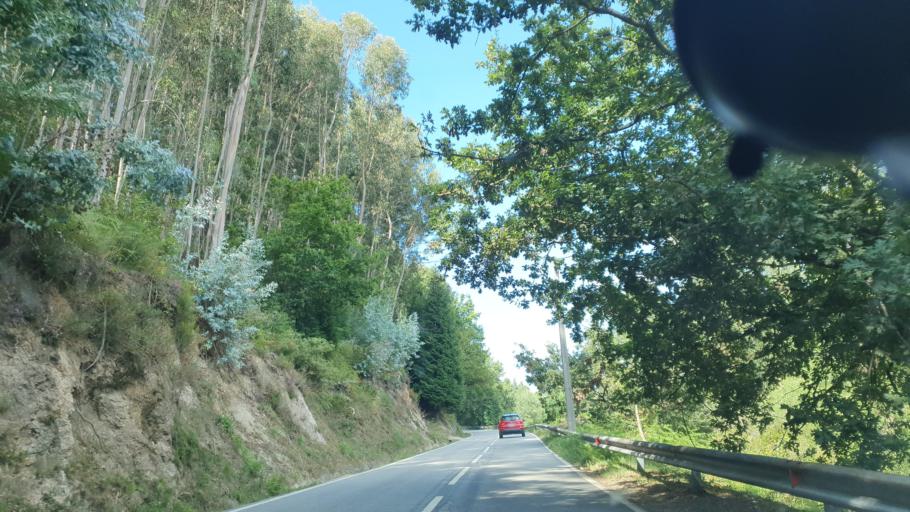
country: PT
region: Braga
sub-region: Vieira do Minho
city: Real
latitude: 41.7192
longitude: -8.2183
